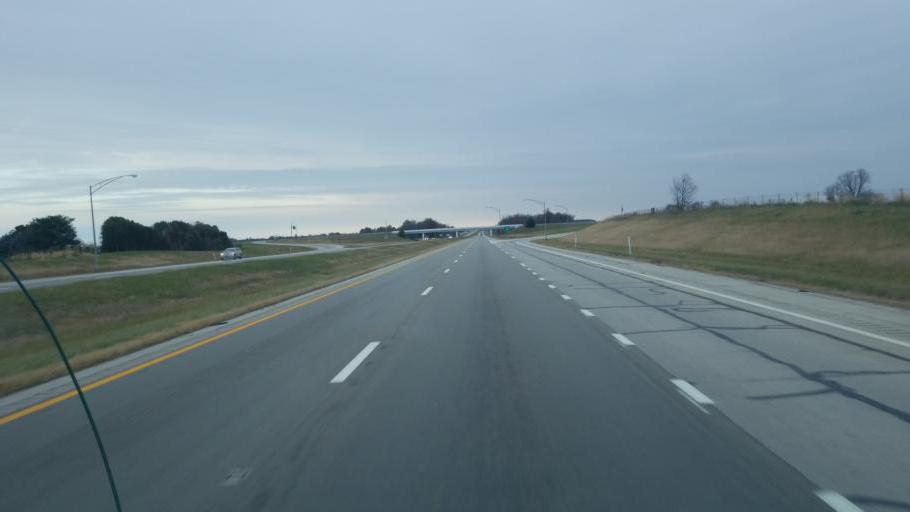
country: US
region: Ohio
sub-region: Auglaize County
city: Saint Marys
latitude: 40.5613
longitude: -84.2932
